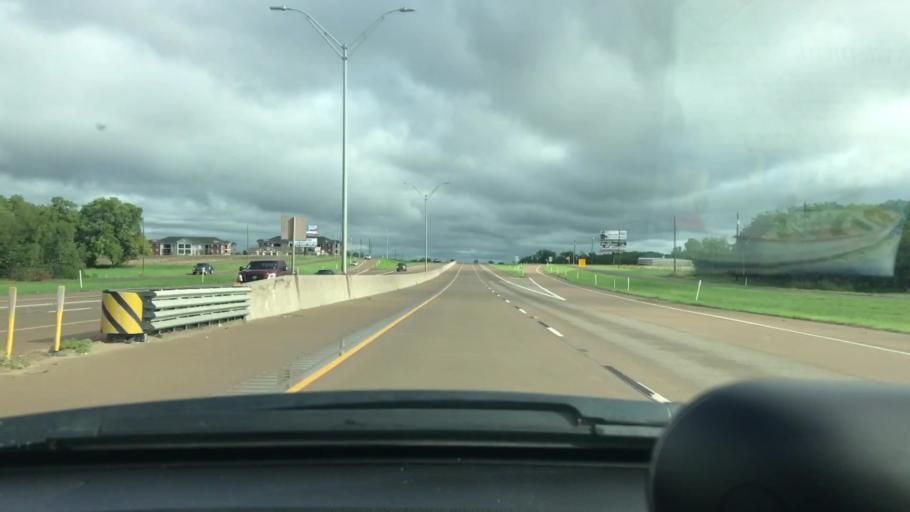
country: US
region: Texas
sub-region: Grayson County
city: Howe
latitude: 33.4896
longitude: -96.6199
